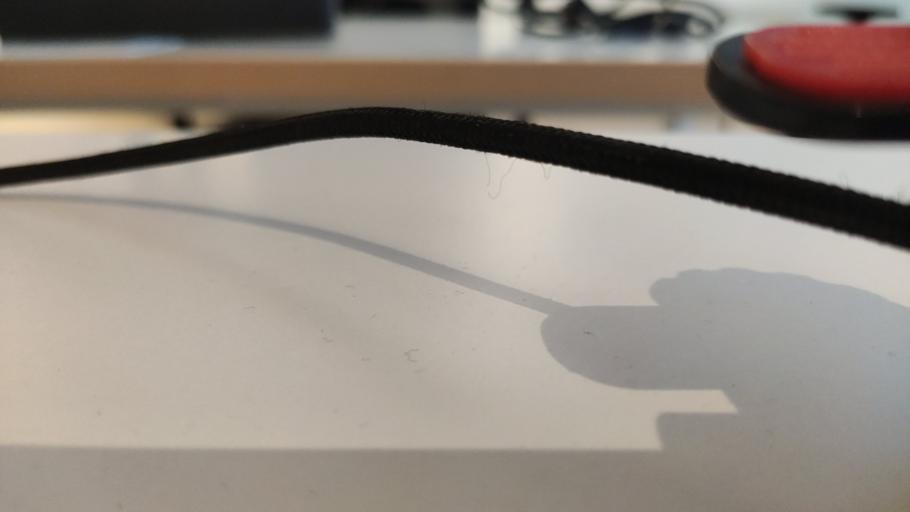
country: RU
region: Moskovskaya
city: Sychevo
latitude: 55.8503
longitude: 36.3568
